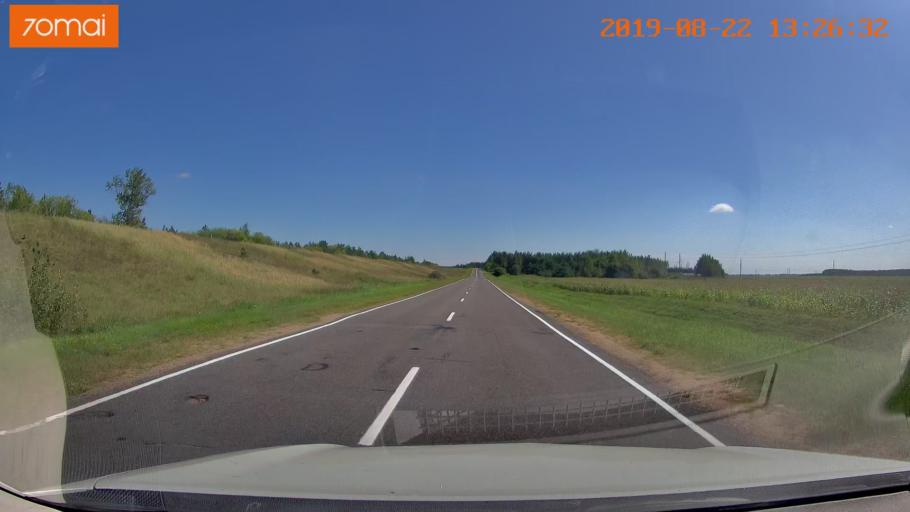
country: BY
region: Minsk
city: Staryya Darohi
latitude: 53.2091
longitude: 28.0645
